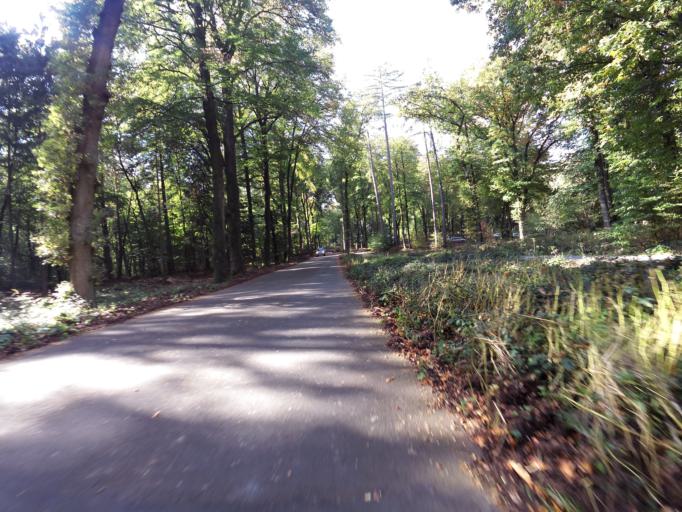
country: NL
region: Gelderland
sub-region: Gemeente Rheden
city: Velp
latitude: 52.0155
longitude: 5.9882
